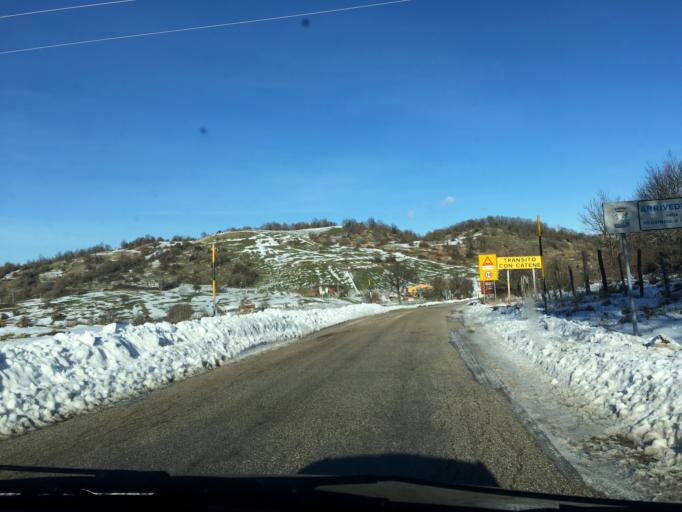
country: IT
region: Abruzzo
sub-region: Provincia di Chieti
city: Rosello
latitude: 41.8637
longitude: 14.3528
